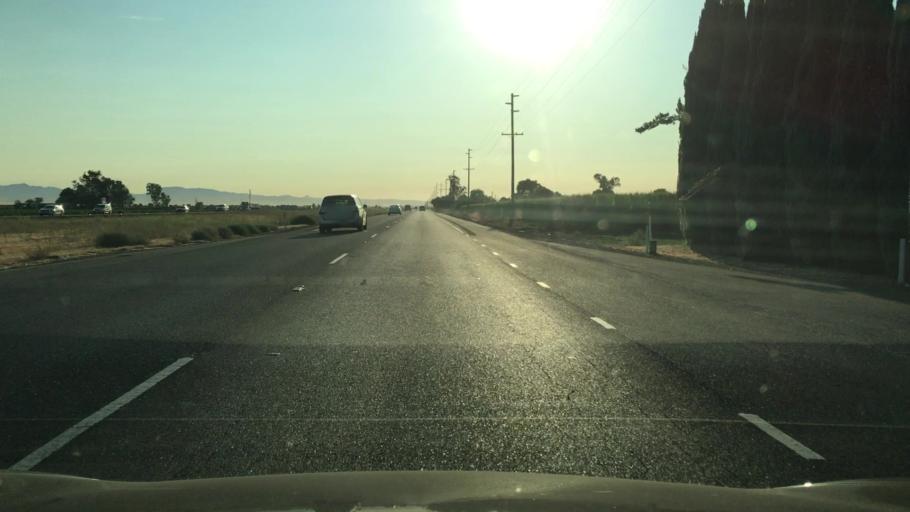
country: US
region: California
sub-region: Merced County
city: South Dos Palos
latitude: 37.0550
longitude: -120.7262
